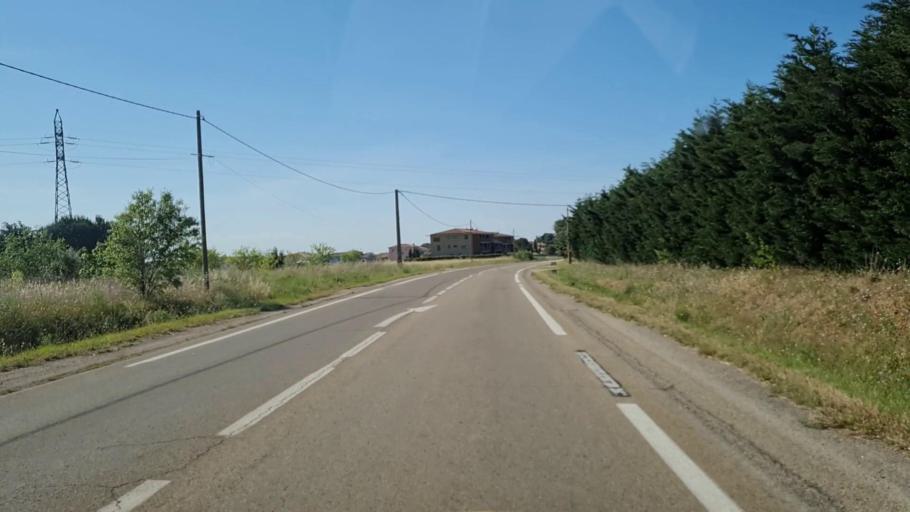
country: FR
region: Languedoc-Roussillon
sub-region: Departement du Gard
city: Saint-Gilles
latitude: 43.7003
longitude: 4.4242
